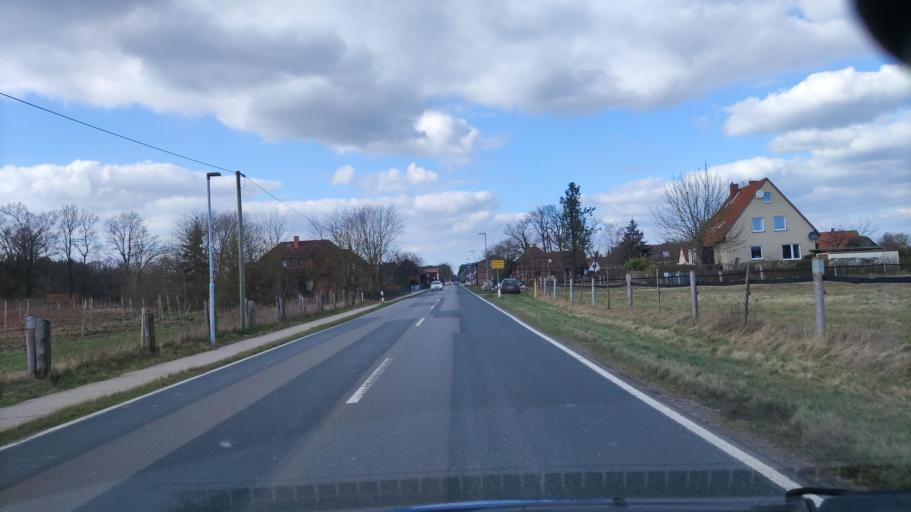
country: DE
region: Lower Saxony
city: Beedenbostel
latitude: 52.6346
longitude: 10.2184
